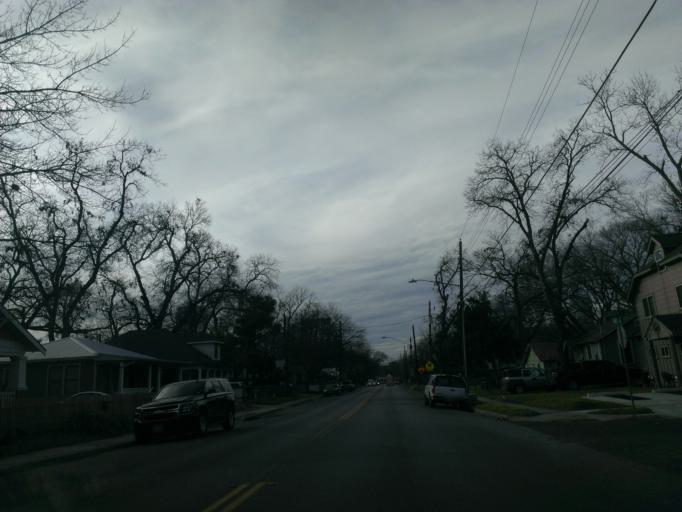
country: US
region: Texas
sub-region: Travis County
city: Austin
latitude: 30.2557
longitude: -97.7325
